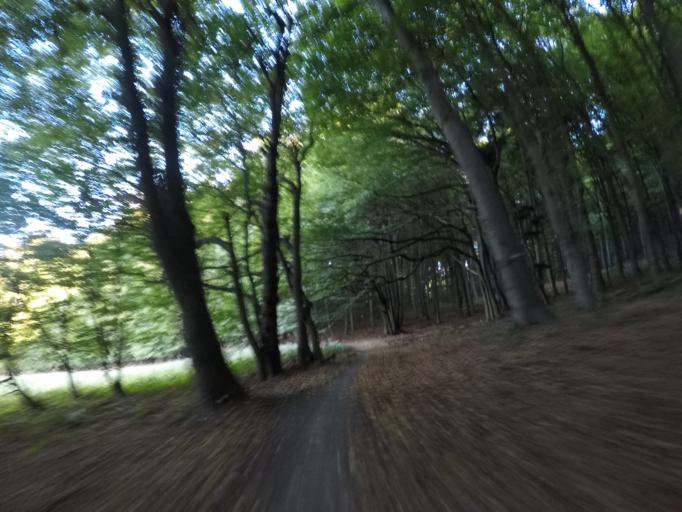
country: SK
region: Kosicky
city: Kosice
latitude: 48.7605
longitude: 21.1453
